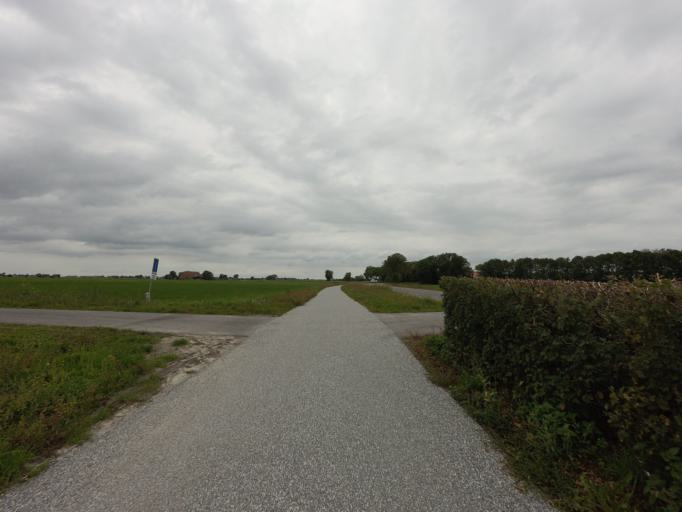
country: NL
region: Friesland
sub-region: Sudwest Fryslan
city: IJlst
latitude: 53.0442
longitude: 5.6146
